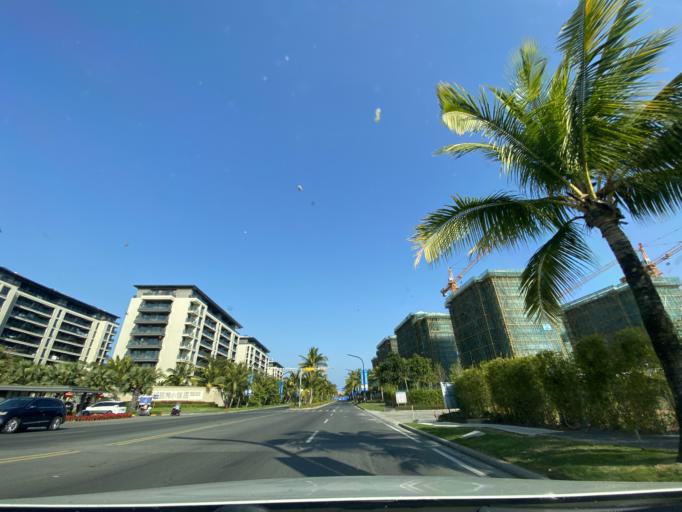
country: CN
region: Hainan
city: Xincun
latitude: 18.4237
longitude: 109.9581
